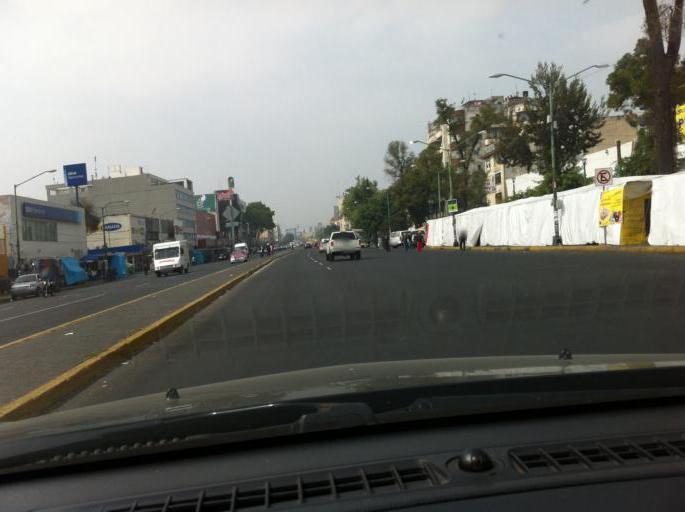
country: MX
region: Mexico City
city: Cuauhtemoc
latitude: 19.4400
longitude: -99.1559
